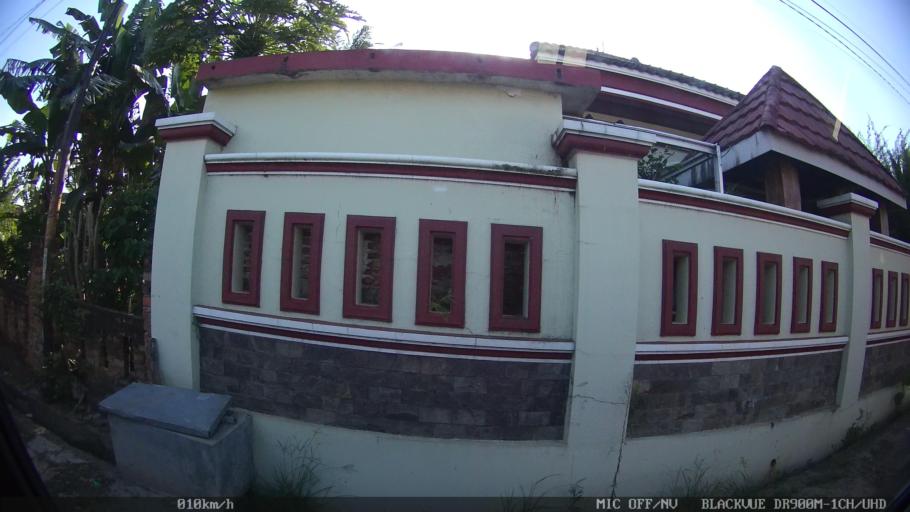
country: ID
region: Lampung
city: Kedaton
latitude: -5.3704
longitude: 105.2309
